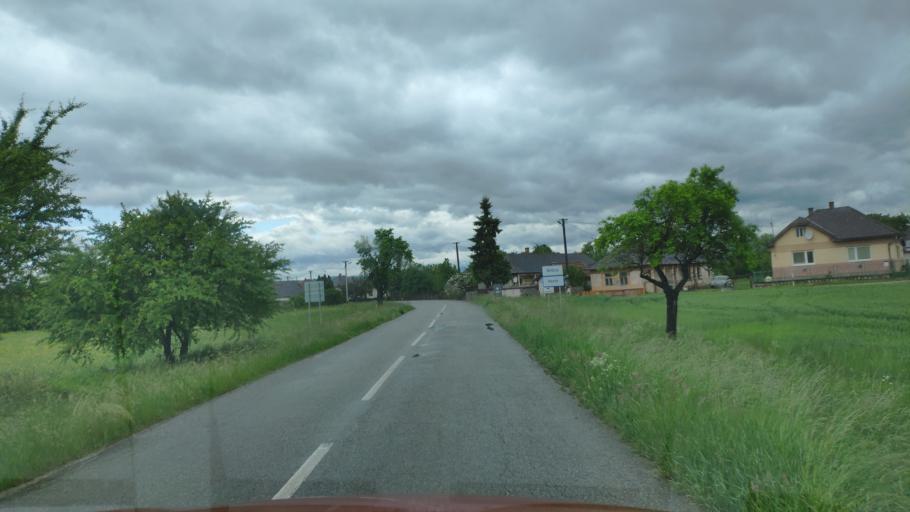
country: SK
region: Kosicky
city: Moldava nad Bodvou
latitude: 48.5417
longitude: 21.0487
